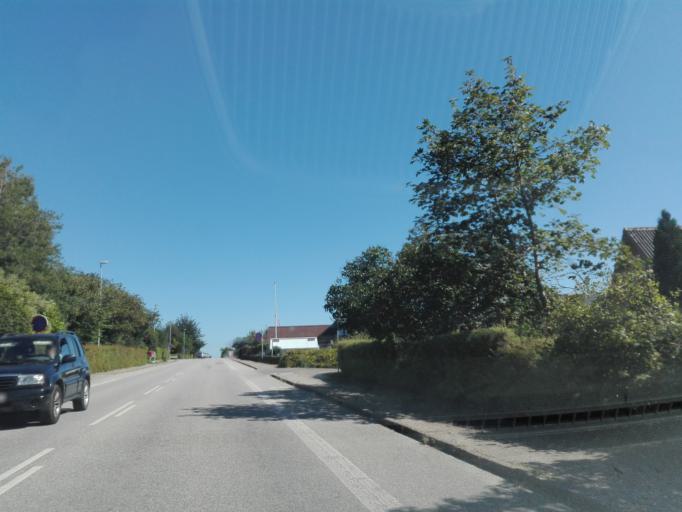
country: DK
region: Central Jutland
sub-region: Arhus Kommune
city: Malling
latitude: 55.9745
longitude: 10.2297
